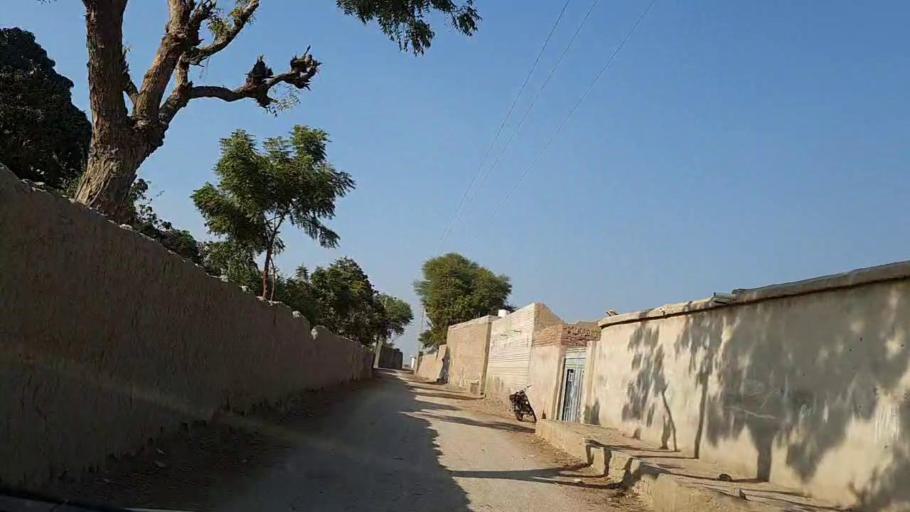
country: PK
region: Sindh
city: Sakrand
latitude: 26.1334
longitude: 68.2374
